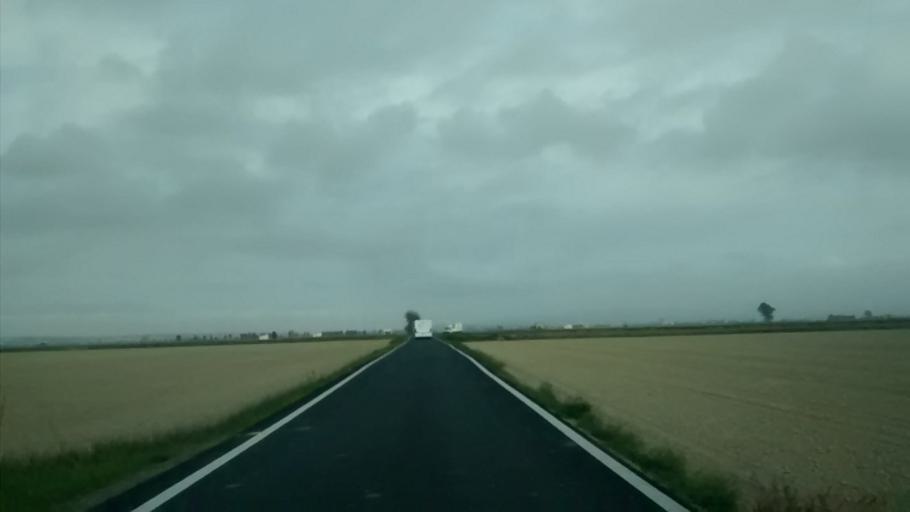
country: ES
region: Catalonia
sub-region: Provincia de Tarragona
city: Deltebre
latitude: 40.6699
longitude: 0.6529
